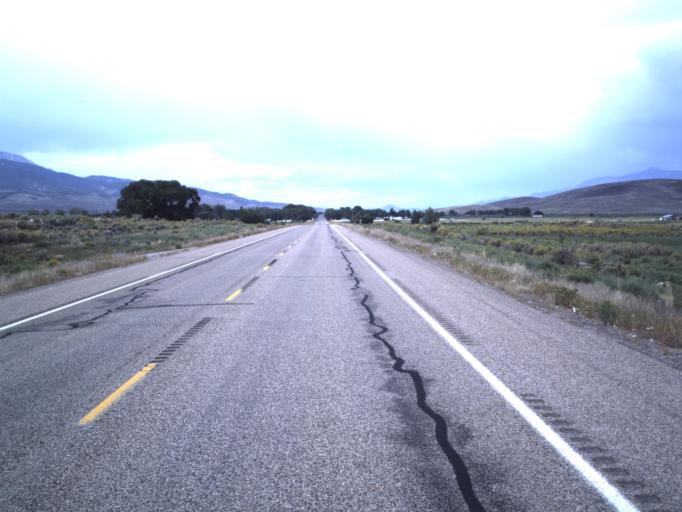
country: US
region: Utah
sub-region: Piute County
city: Junction
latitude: 38.2205
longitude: -112.2197
